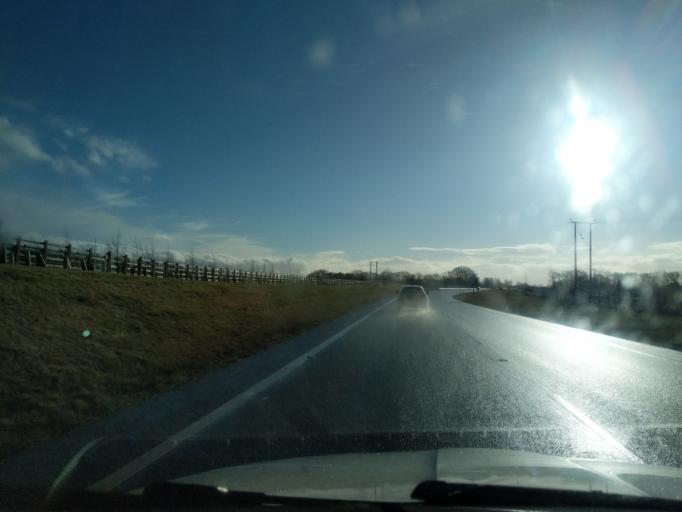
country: GB
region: England
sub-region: North Yorkshire
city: Bedale
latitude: 54.2984
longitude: -1.5889
